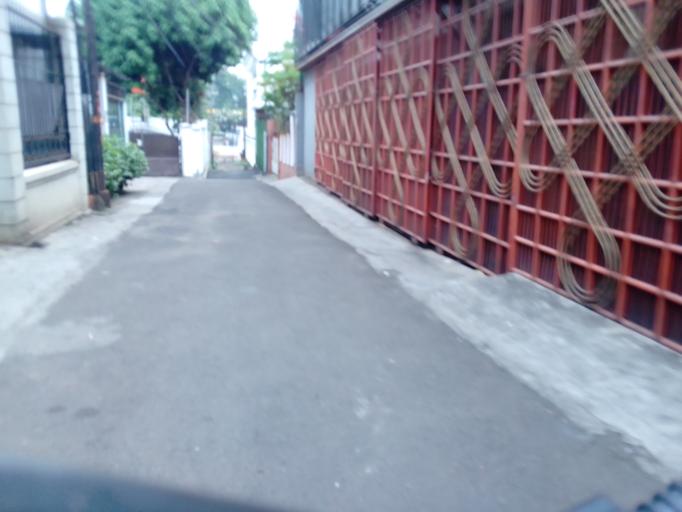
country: ID
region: Jakarta Raya
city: Jakarta
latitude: -6.2148
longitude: 106.8104
